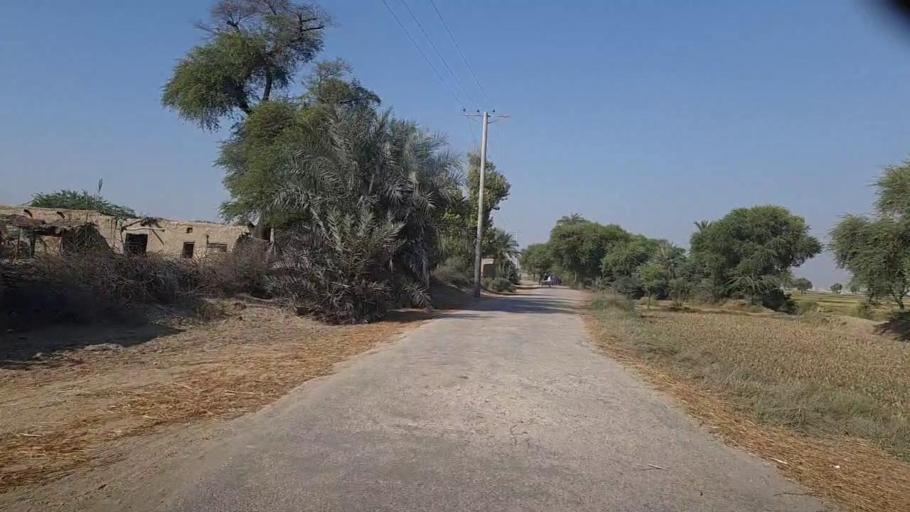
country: PK
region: Sindh
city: Tangwani
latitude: 28.2456
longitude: 68.9963
